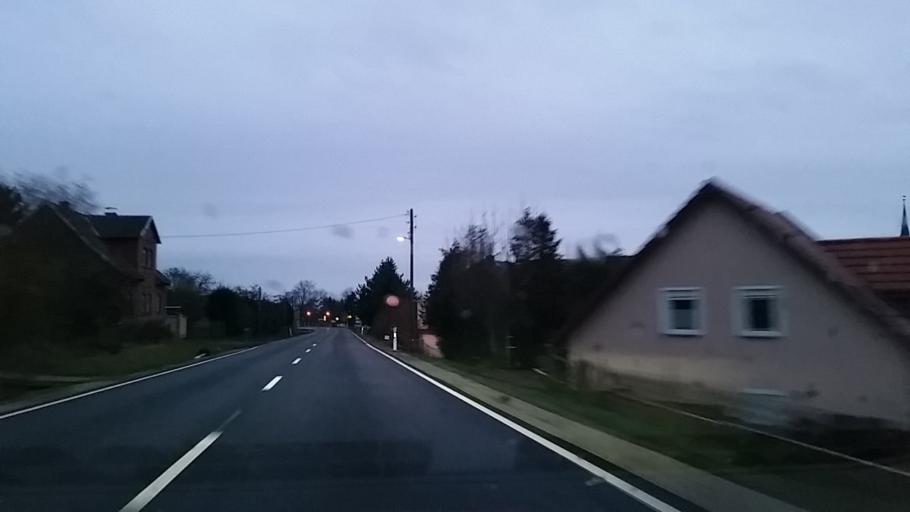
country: DE
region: Thuringia
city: Sondershausen
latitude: 51.3148
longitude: 10.8539
